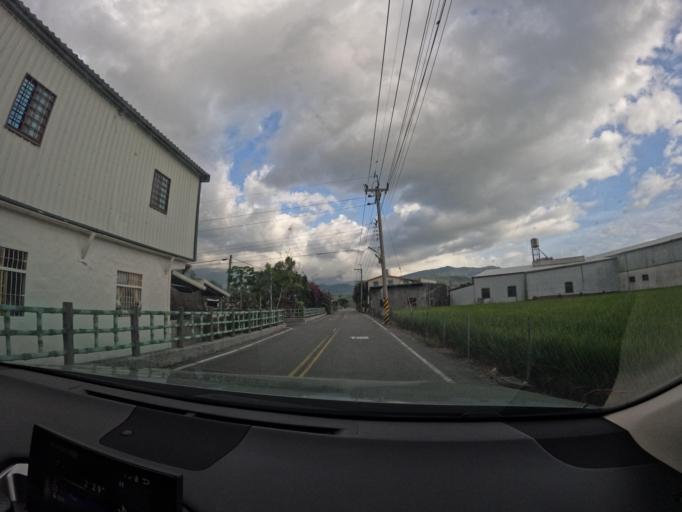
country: TW
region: Taiwan
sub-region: Taitung
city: Taitung
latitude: 23.1537
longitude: 121.2250
